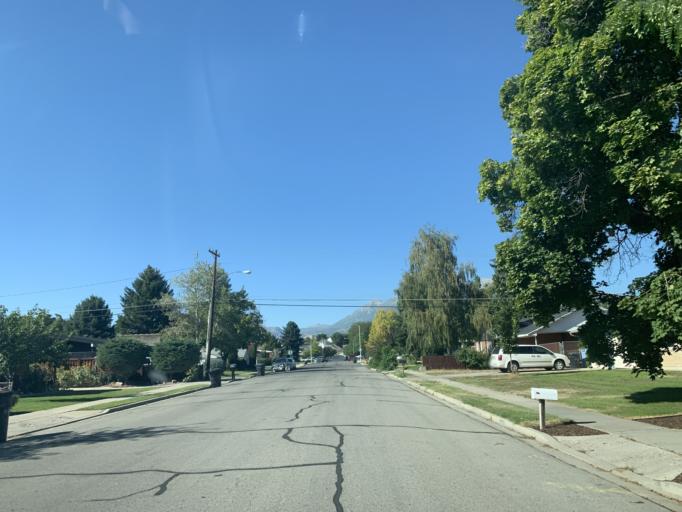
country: US
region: Utah
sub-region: Utah County
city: Provo
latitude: 40.2557
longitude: -111.6820
